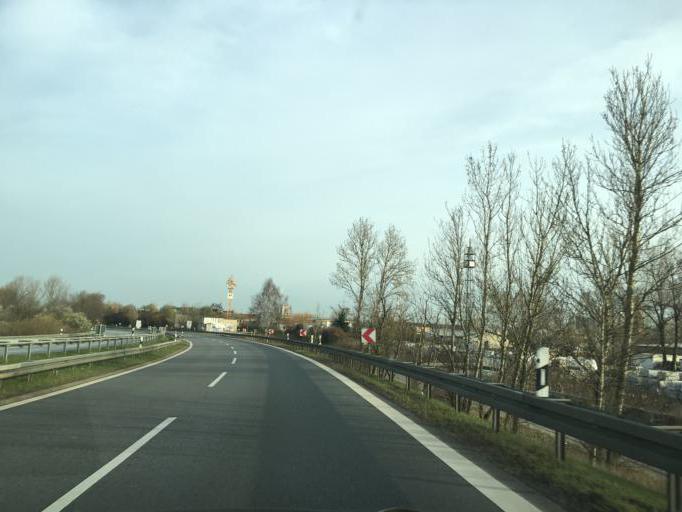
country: DE
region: Berlin
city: Buchholz
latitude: 52.6465
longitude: 13.4260
